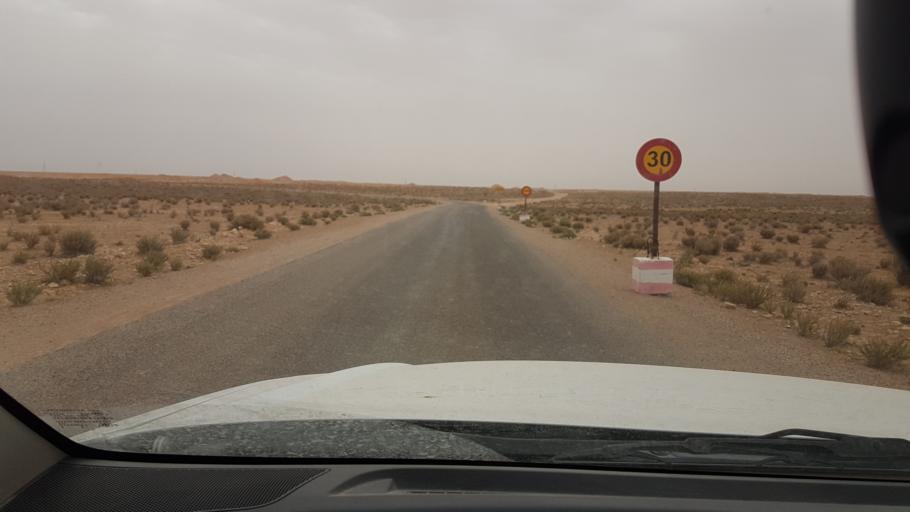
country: TN
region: Madanin
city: Medenine
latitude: 33.2872
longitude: 10.5950
